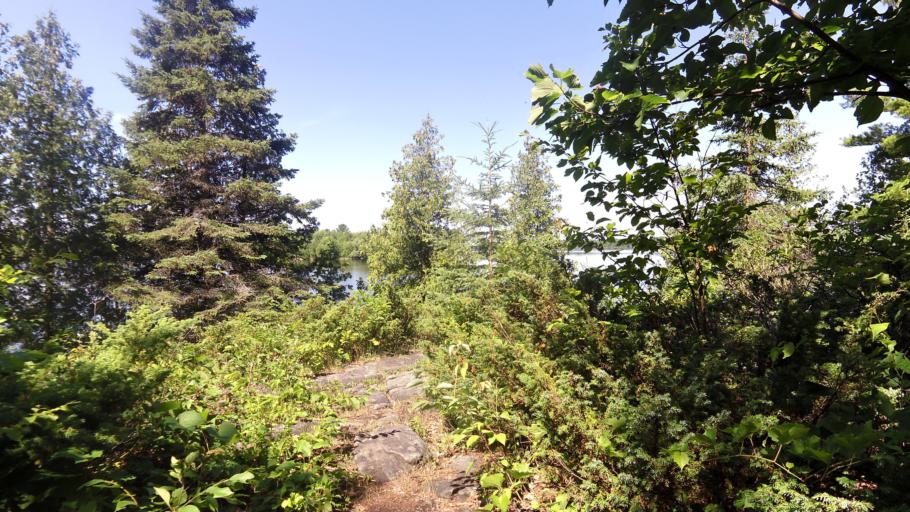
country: CA
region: Ontario
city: Arnprior
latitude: 45.4644
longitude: -76.2652
